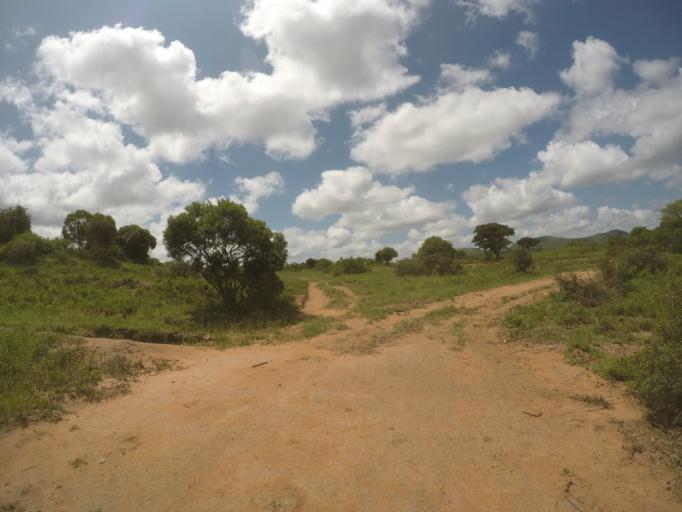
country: ZA
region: KwaZulu-Natal
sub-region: uThungulu District Municipality
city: Empangeni
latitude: -28.5809
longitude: 31.8428
